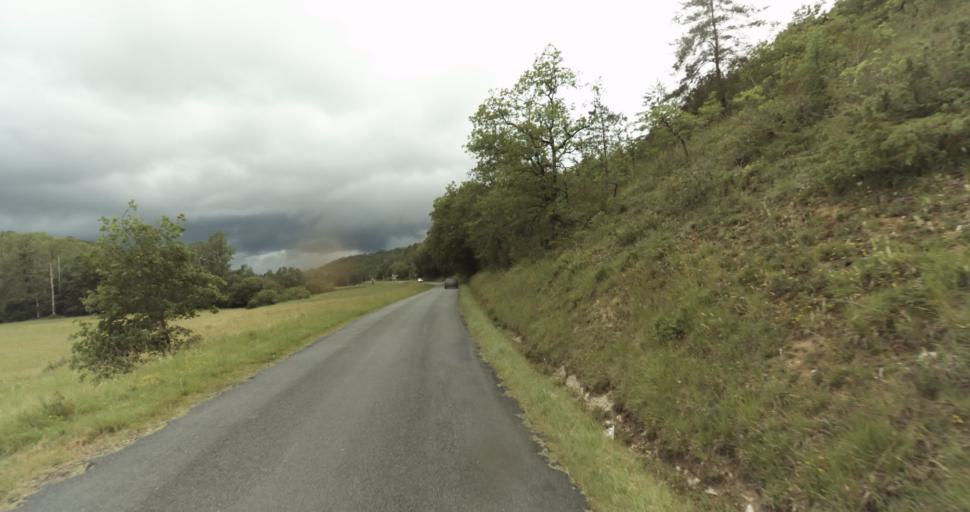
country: FR
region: Aquitaine
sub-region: Departement de la Dordogne
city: Beaumont-du-Perigord
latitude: 44.7513
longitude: 0.8431
